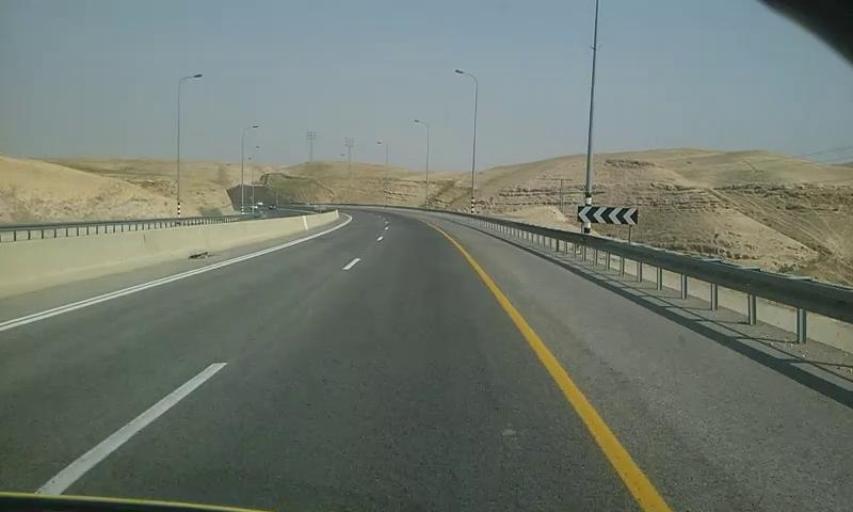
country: PS
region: West Bank
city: Jericho
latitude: 31.7988
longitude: 35.4340
